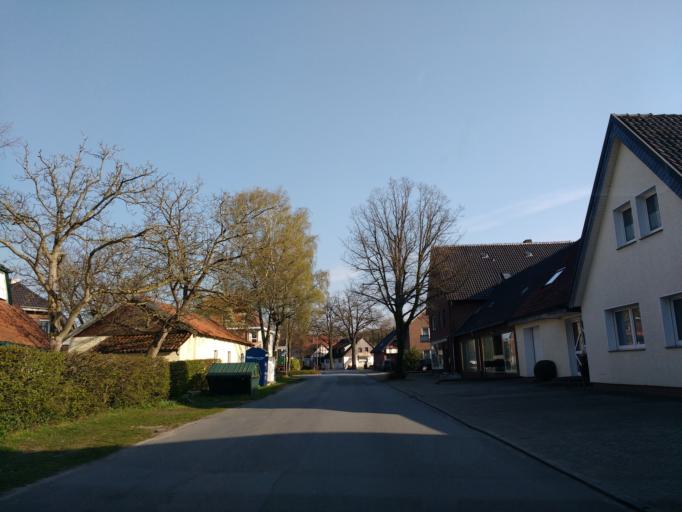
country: DE
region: Lower Saxony
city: Dissen
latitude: 52.0753
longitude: 8.2000
